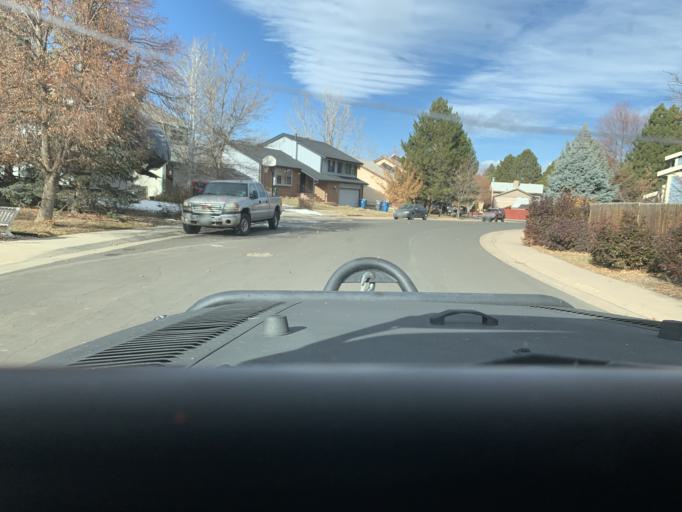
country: US
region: Colorado
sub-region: Adams County
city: Aurora
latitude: 39.7034
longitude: -104.8003
